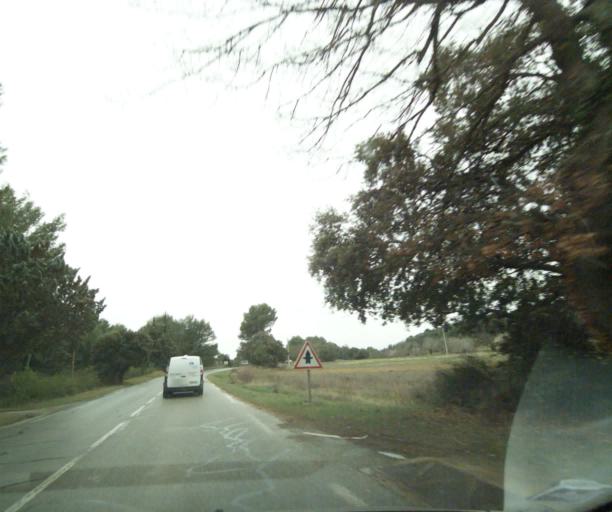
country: FR
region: Provence-Alpes-Cote d'Azur
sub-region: Departement des Bouches-du-Rhone
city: Saint-Cannat
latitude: 43.6611
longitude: 5.3062
